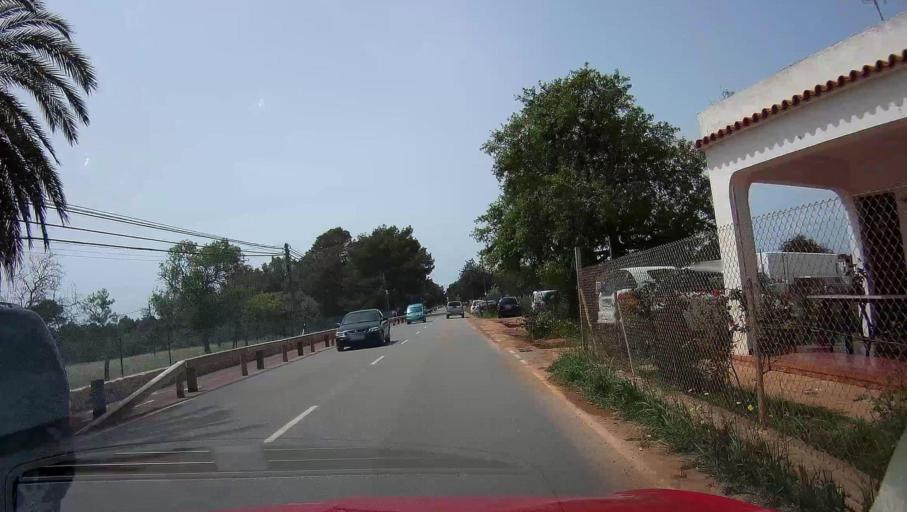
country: ES
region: Balearic Islands
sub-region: Illes Balears
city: Santa Eularia des Riu
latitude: 39.0021
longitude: 1.5663
